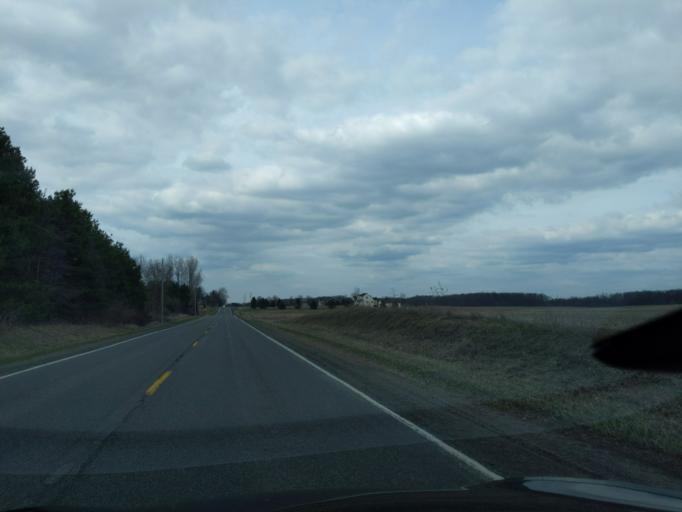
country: US
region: Michigan
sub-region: Ingham County
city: Mason
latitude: 42.5848
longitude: -84.4835
